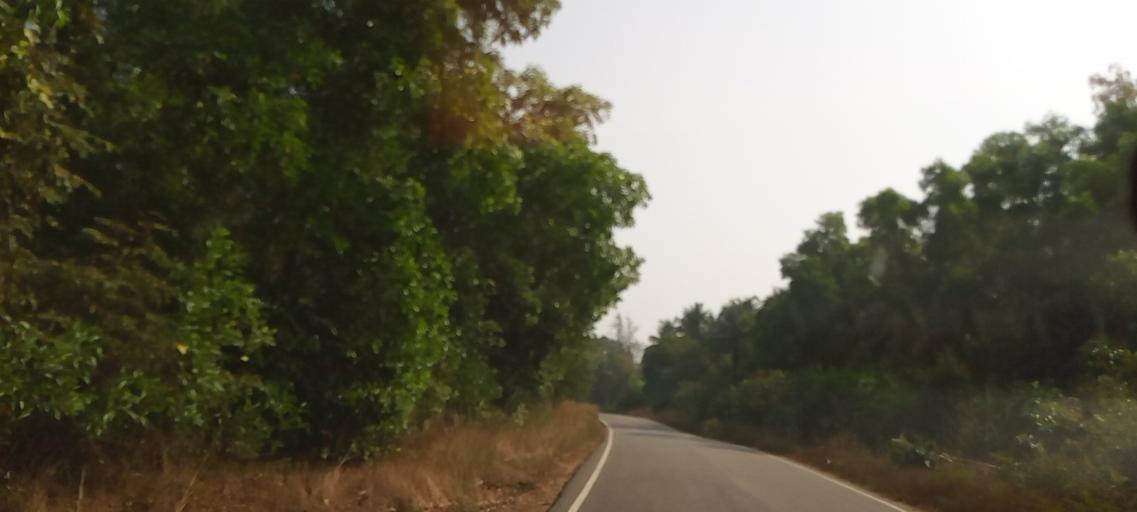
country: IN
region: Karnataka
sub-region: Udupi
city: Coondapoor
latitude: 13.5136
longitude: 74.7853
